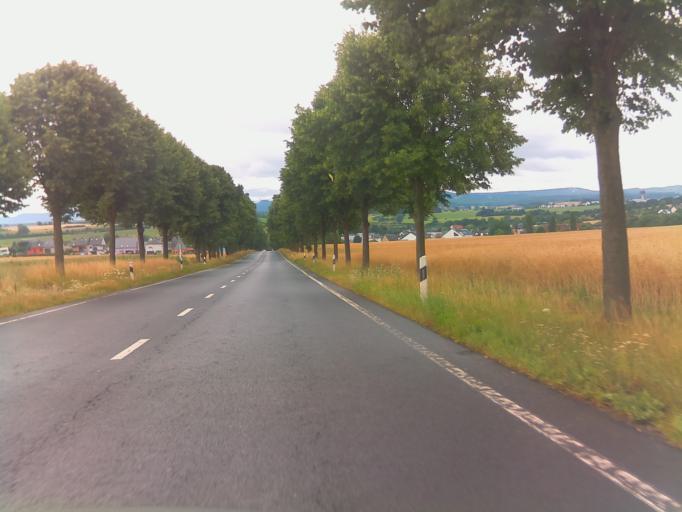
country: LU
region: Luxembourg
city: Aspelt
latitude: 49.5282
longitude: 6.2375
